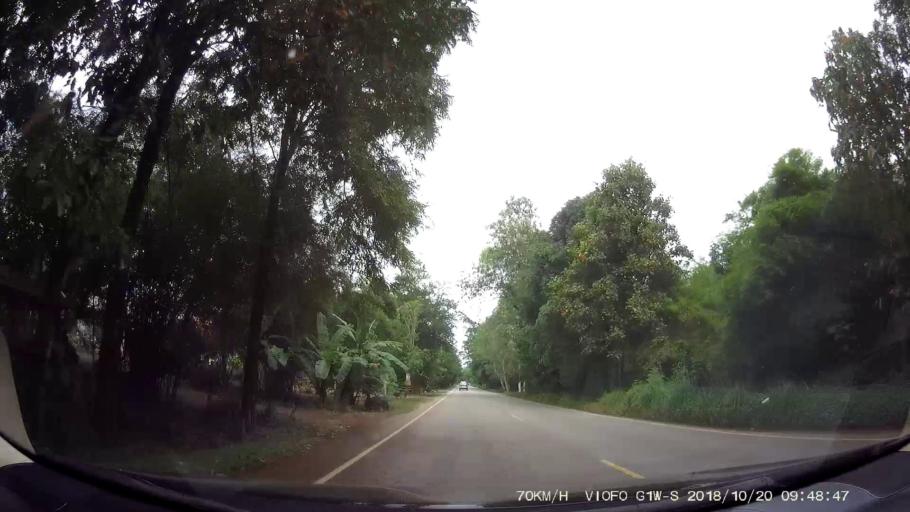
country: TH
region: Chaiyaphum
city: Khon San
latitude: 16.5140
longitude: 101.9093
